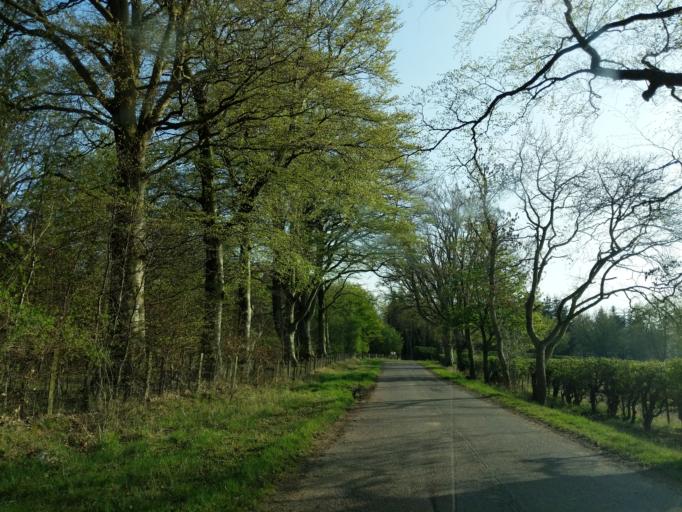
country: GB
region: Scotland
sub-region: Fife
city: Pathhead
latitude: 55.8576
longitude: -2.9323
